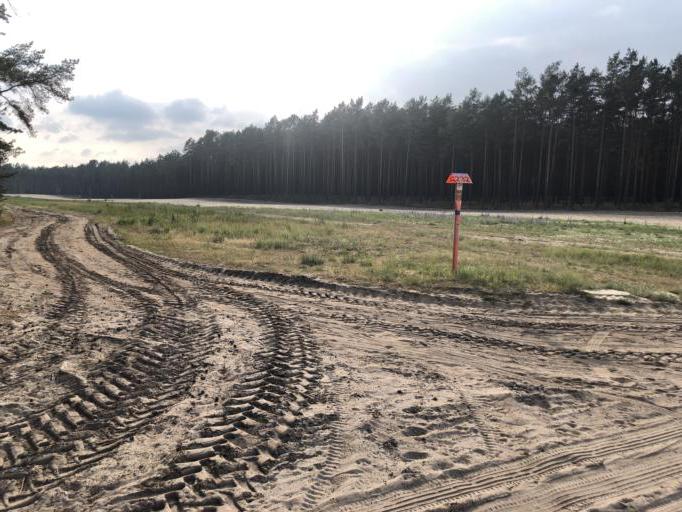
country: DE
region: Brandenburg
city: Bestensee
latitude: 52.2172
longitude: 13.6625
